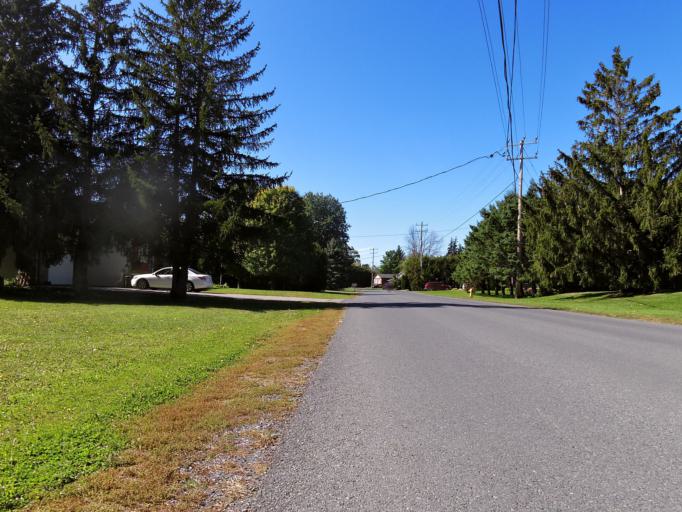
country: CA
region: Ontario
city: Casselman
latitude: 45.2691
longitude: -75.2754
